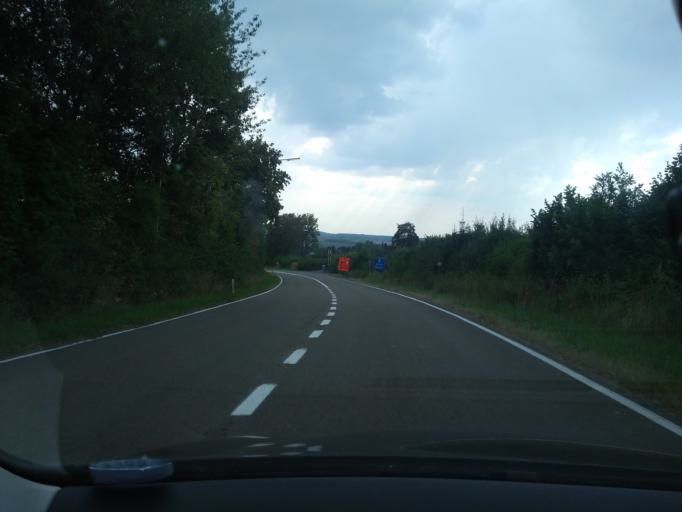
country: BE
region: Wallonia
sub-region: Province du Luxembourg
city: Sainte-Ode
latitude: 50.0476
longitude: 5.5705
